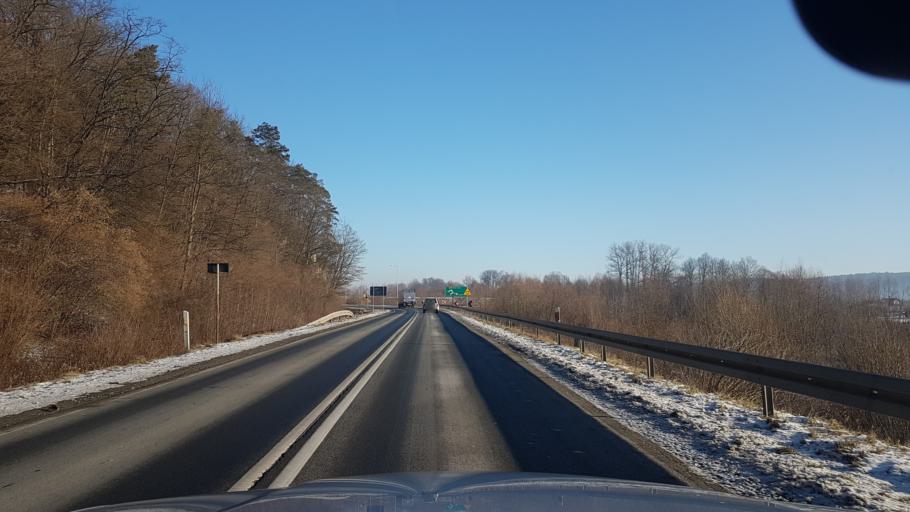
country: PL
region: Lesser Poland Voivodeship
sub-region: Powiat nowosadecki
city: Podegrodzie
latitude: 49.5484
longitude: 20.5671
